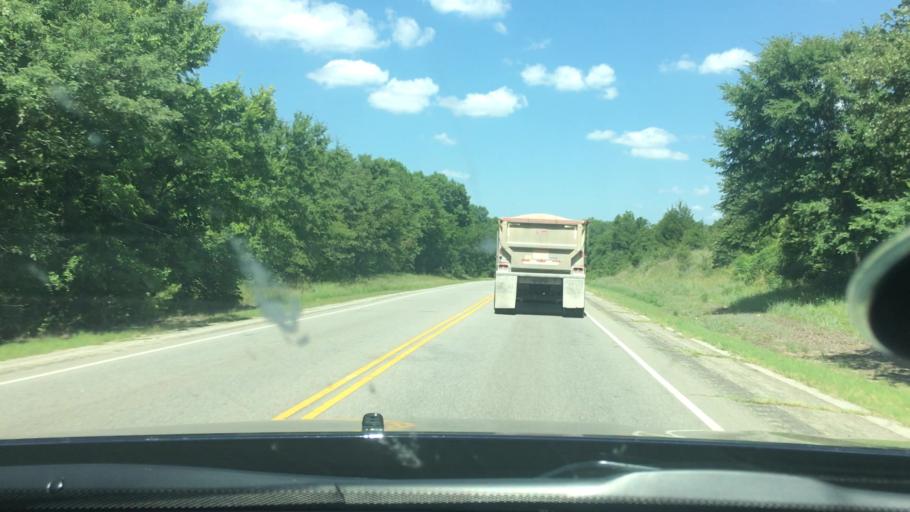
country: US
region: Oklahoma
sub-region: Marshall County
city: Oakland
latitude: 34.1657
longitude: -96.8296
